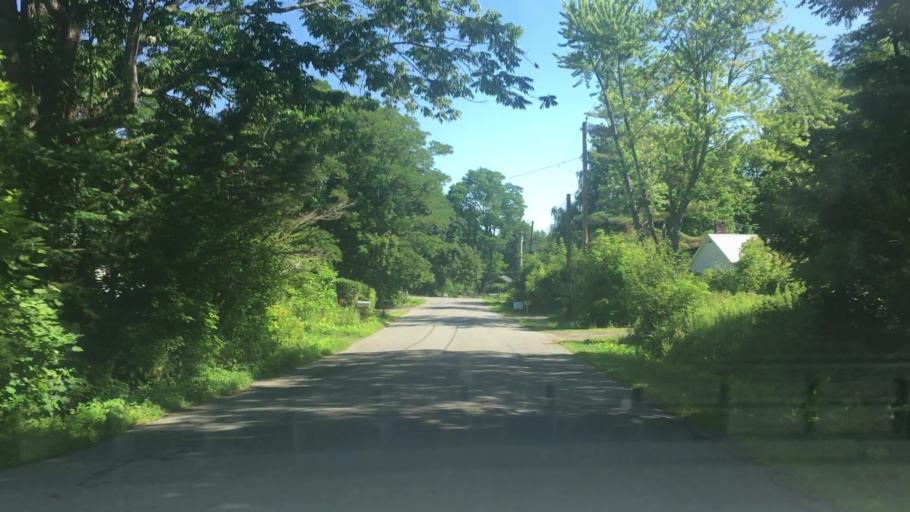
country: US
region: Maine
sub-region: Waldo County
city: Northport
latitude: 44.3812
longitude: -68.9810
